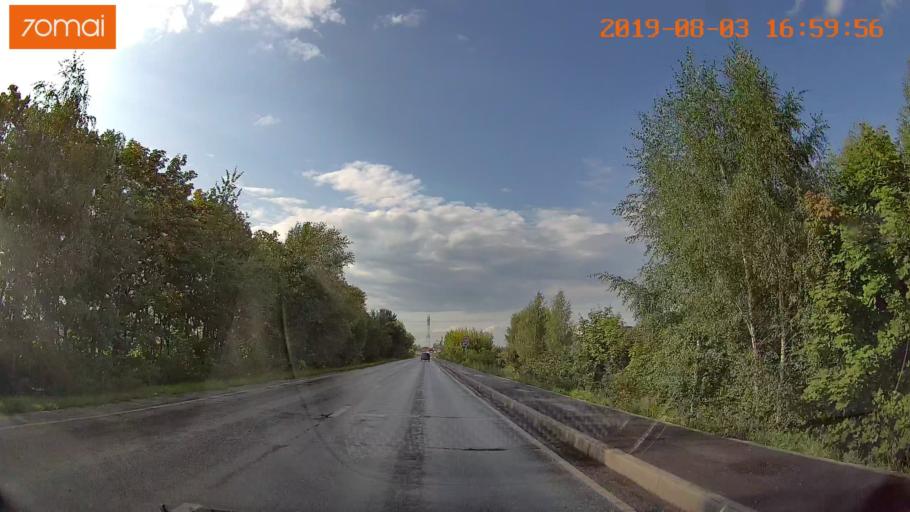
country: RU
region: Moskovskaya
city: Voskresensk
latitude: 55.3333
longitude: 38.6210
